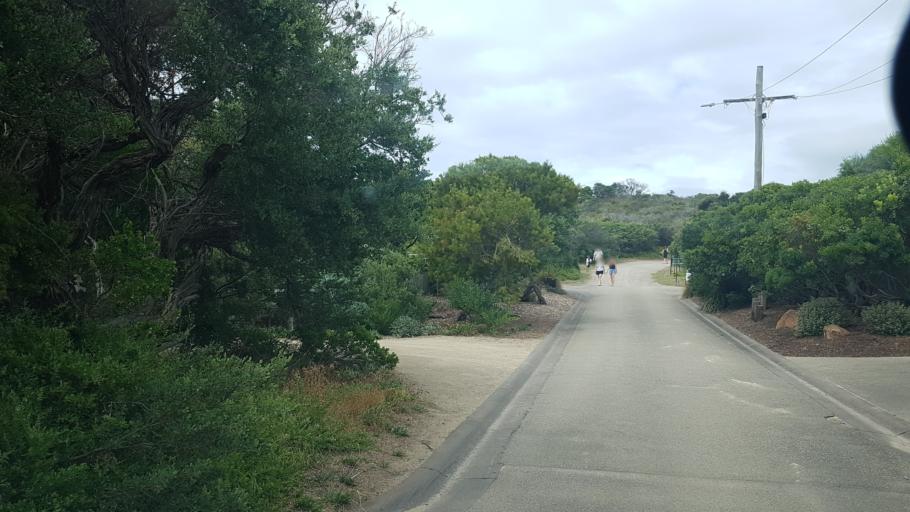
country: AU
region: Victoria
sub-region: Mornington Peninsula
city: Blairgowrie
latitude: -38.3793
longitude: 144.7775
